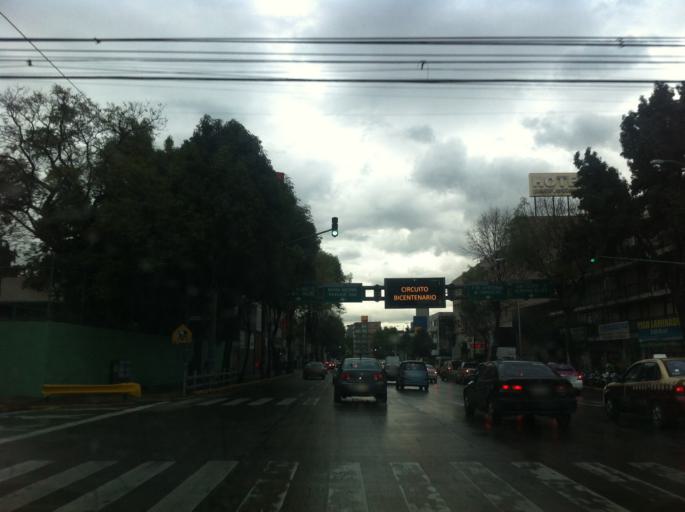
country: MX
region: Mexico City
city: Benito Juarez
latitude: 19.4025
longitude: -99.1793
